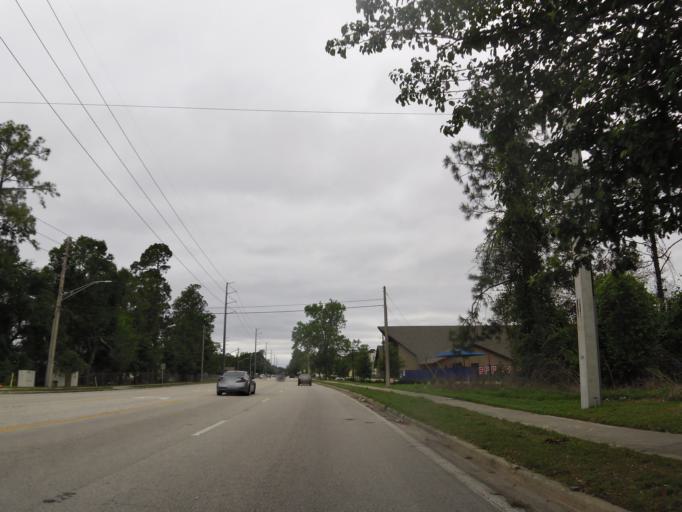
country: US
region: Florida
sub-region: Saint Johns County
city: Fruit Cove
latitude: 30.1753
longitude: -81.6041
